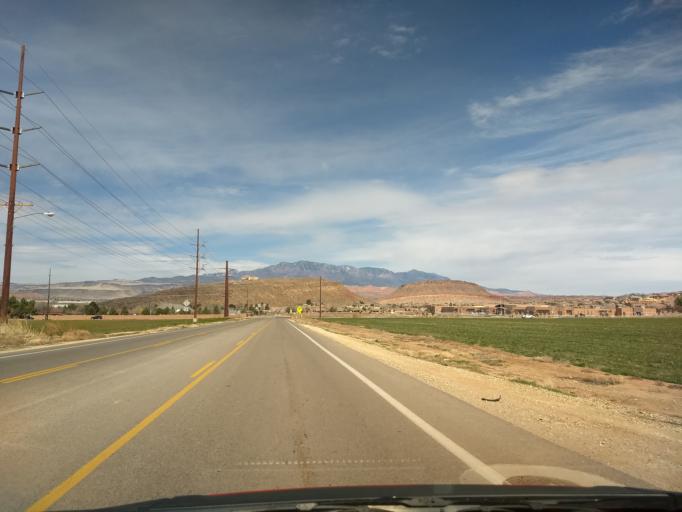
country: US
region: Utah
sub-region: Washington County
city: Washington
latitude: 37.0867
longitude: -113.4996
